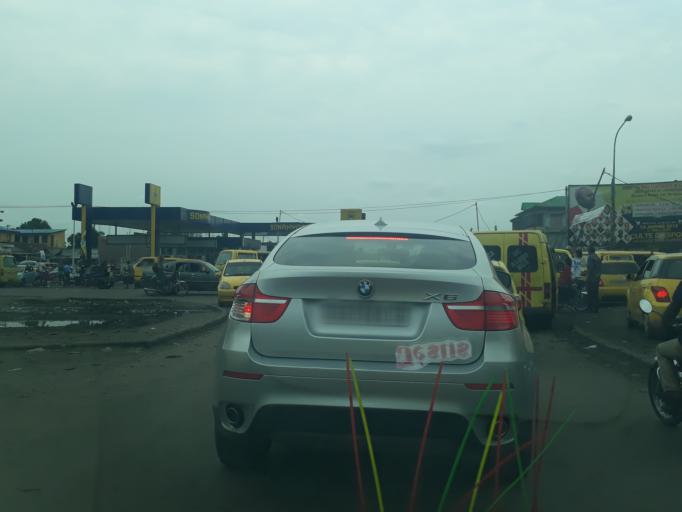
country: CD
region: Kinshasa
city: Kinshasa
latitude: -4.3506
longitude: 15.3009
